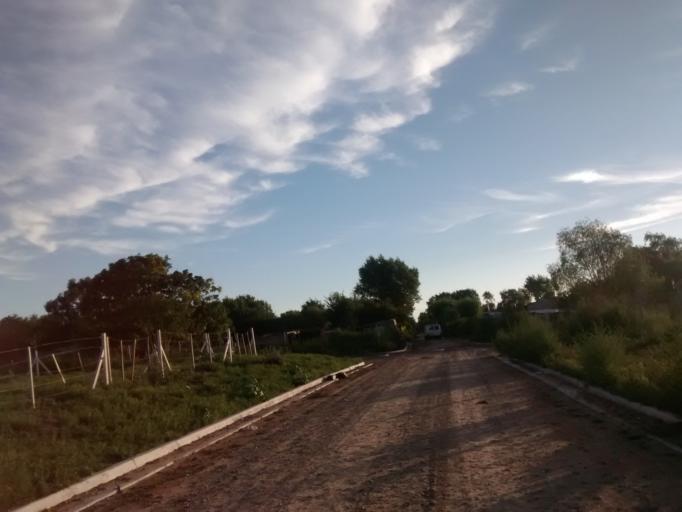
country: AR
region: Buenos Aires
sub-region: Partido de La Plata
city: La Plata
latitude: -34.9539
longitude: -57.9378
